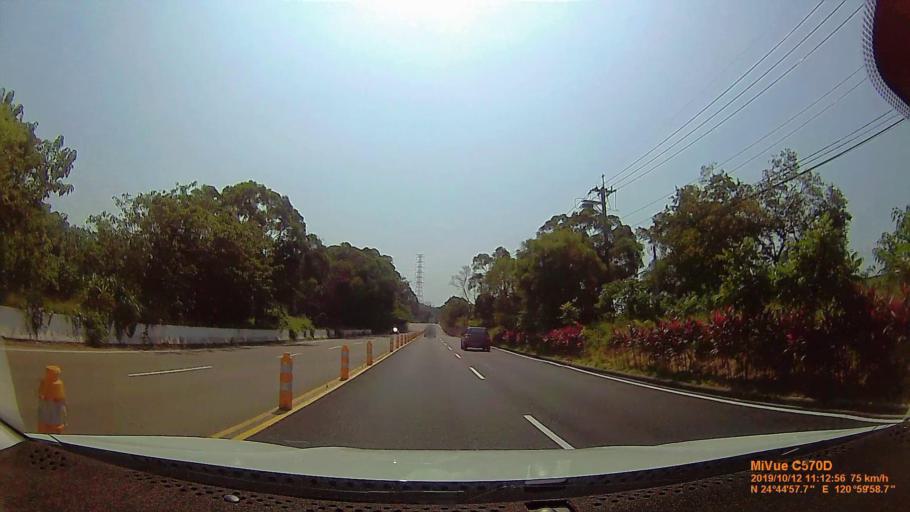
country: TW
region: Taiwan
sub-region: Hsinchu
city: Hsinchu
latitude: 24.7492
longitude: 121.0000
